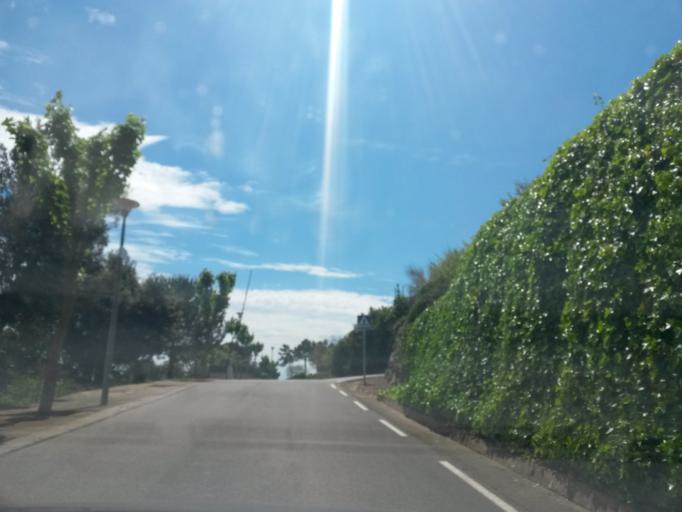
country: ES
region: Catalonia
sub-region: Provincia de Girona
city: Vilablareix
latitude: 41.9631
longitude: 2.7611
